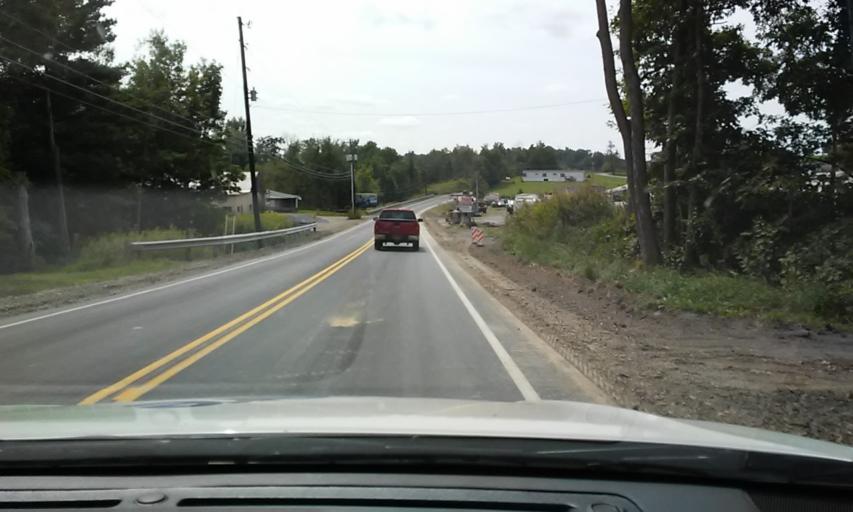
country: US
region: Pennsylvania
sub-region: Clearfield County
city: Treasure Lake
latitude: 41.1714
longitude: -78.6521
